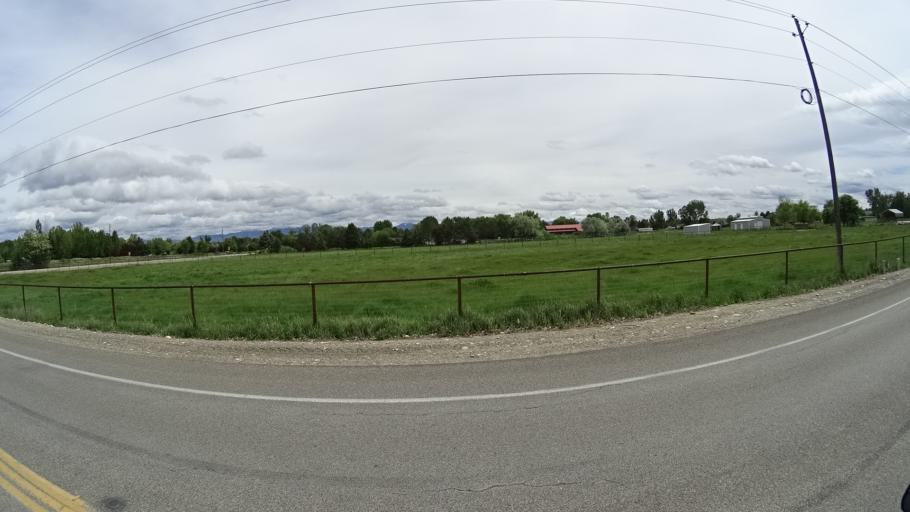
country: US
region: Idaho
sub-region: Ada County
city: Eagle
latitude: 43.6839
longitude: -116.4139
